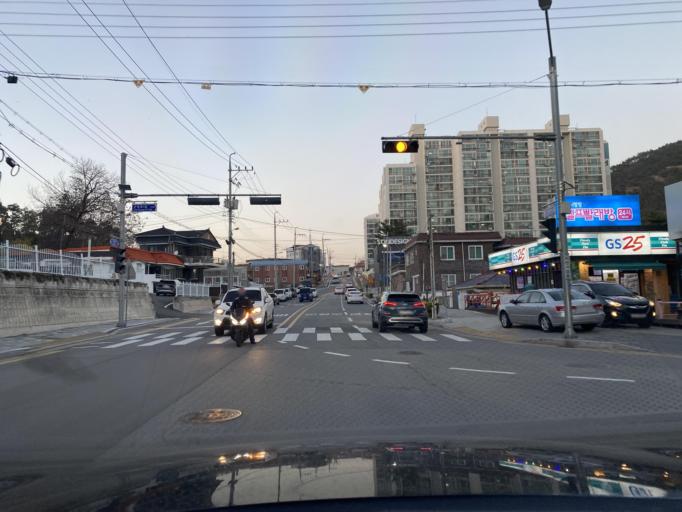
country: KR
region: Chungcheongnam-do
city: Yesan
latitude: 36.6828
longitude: 126.8436
